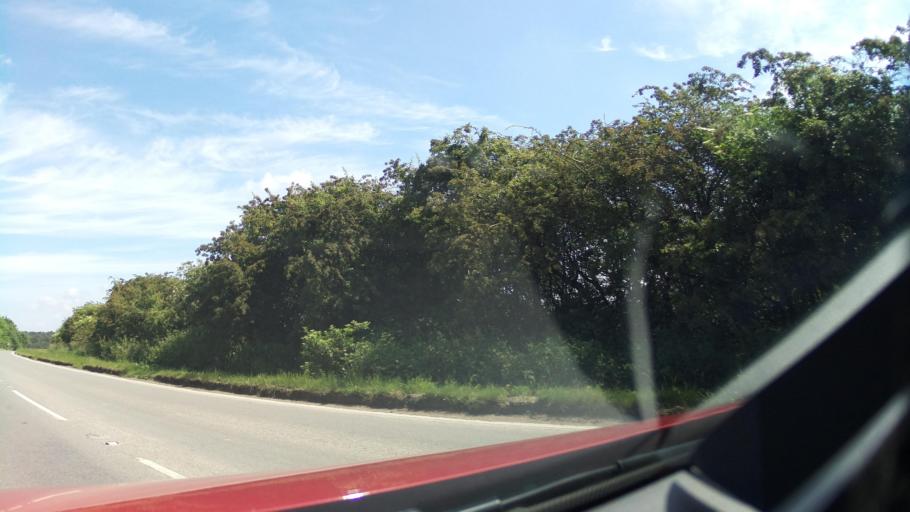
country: GB
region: England
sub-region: North Lincolnshire
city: Manton
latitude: 53.5106
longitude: -0.5818
